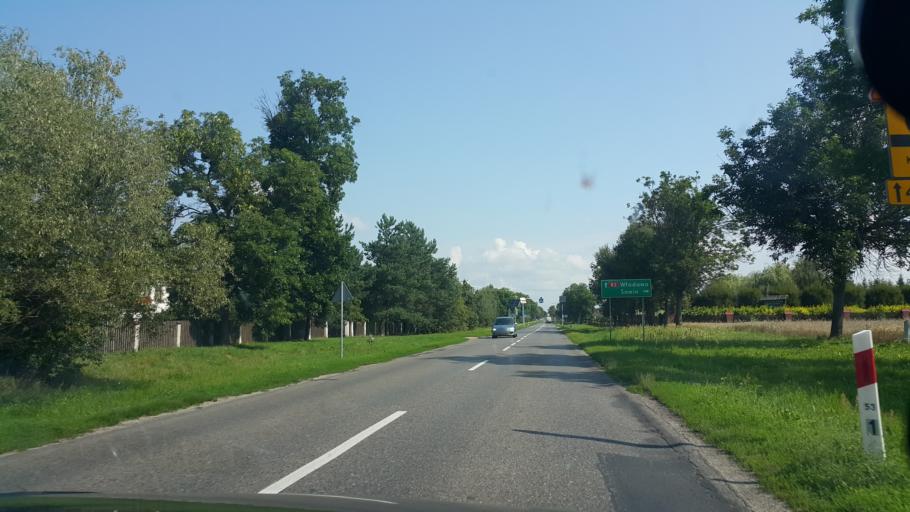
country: PL
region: Lublin Voivodeship
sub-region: Powiat wlodawski
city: Urszulin
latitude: 51.3863
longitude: 23.1905
